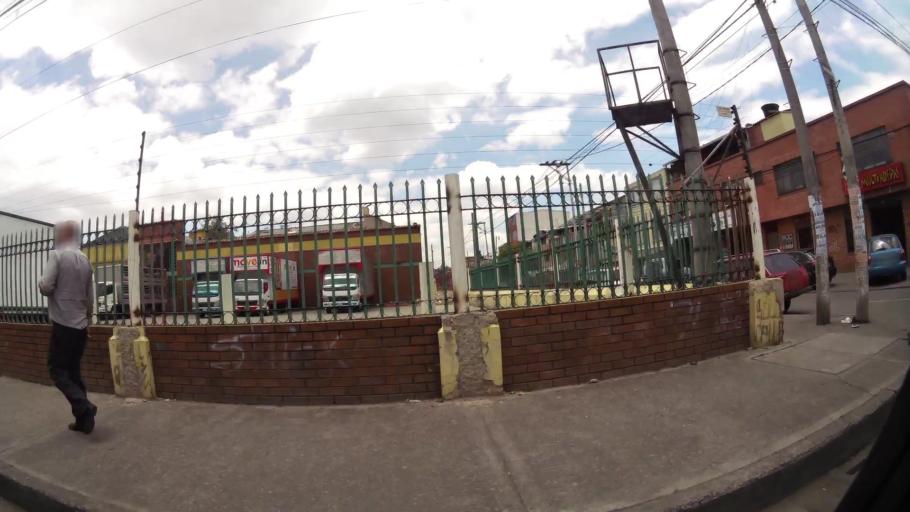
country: CO
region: Bogota D.C.
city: Barrio San Luis
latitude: 4.7174
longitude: -74.0549
